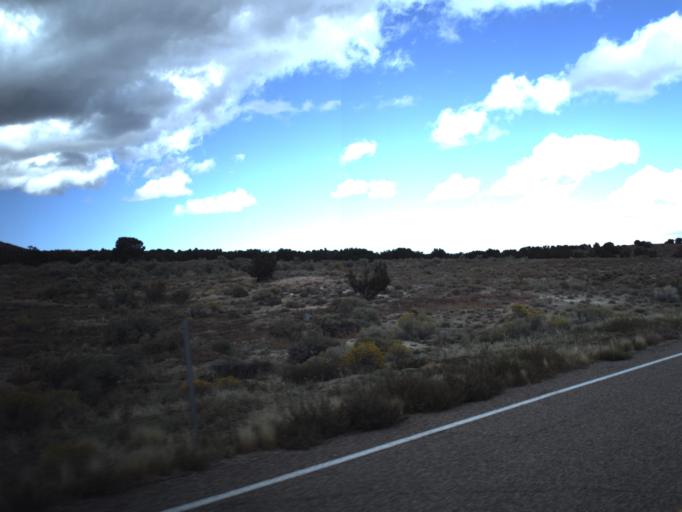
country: US
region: Utah
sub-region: Beaver County
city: Milford
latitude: 38.4582
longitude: -113.2557
